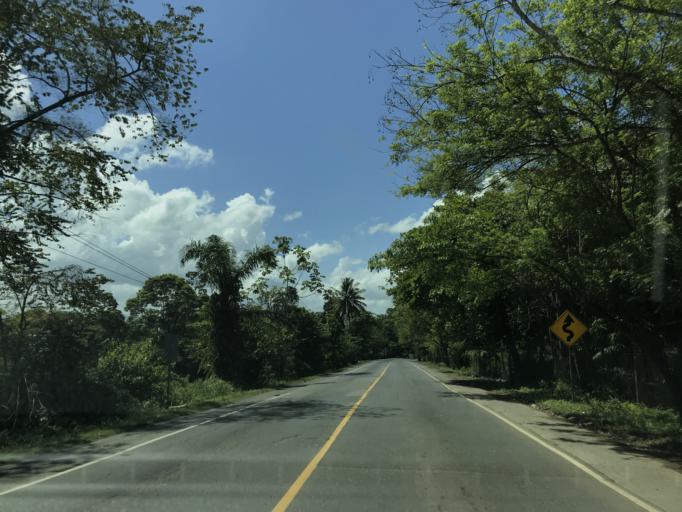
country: GT
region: Izabal
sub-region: Municipio de Puerto Barrios
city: Puerto Barrios
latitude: 15.6592
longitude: -88.5497
